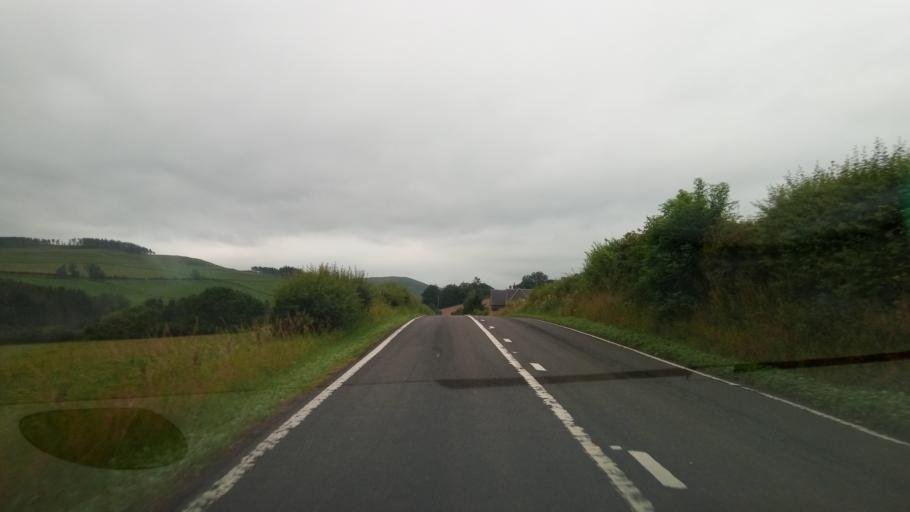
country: GB
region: Scotland
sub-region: The Scottish Borders
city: Hawick
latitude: 55.3725
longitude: -2.8776
